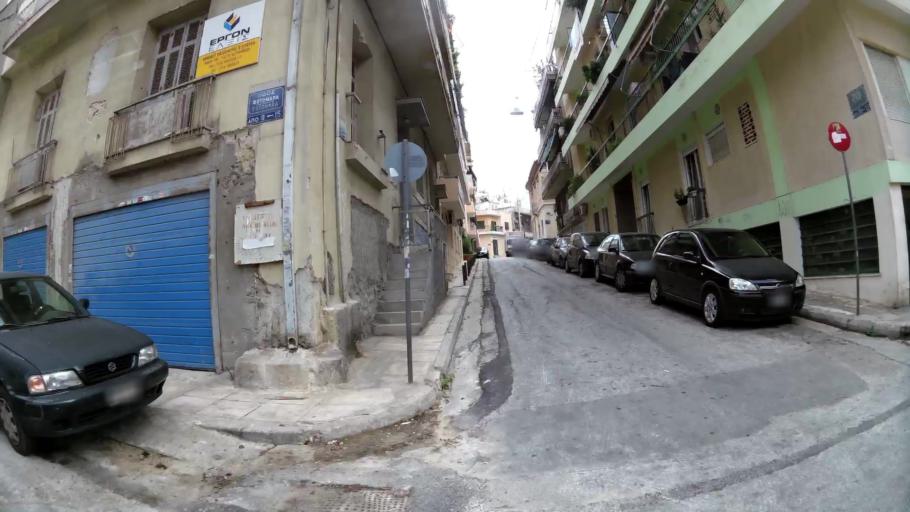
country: GR
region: Attica
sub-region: Nomarchia Athinas
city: Dhafni
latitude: 37.9636
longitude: 23.7294
